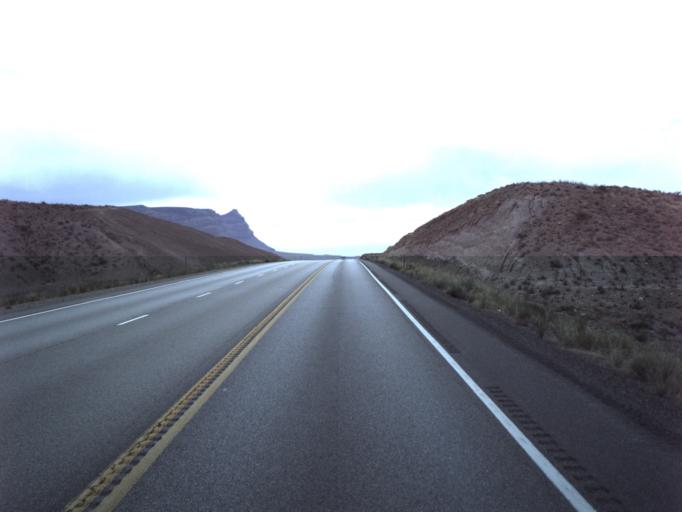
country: US
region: Utah
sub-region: Carbon County
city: East Carbon City
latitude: 39.2820
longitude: -110.3497
